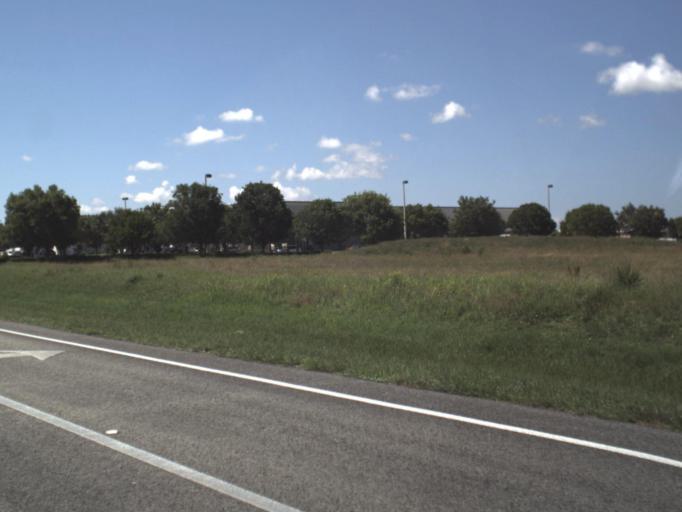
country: US
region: Florida
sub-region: Lee County
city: Lochmoor Waterway Estates
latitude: 26.6734
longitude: -81.9295
